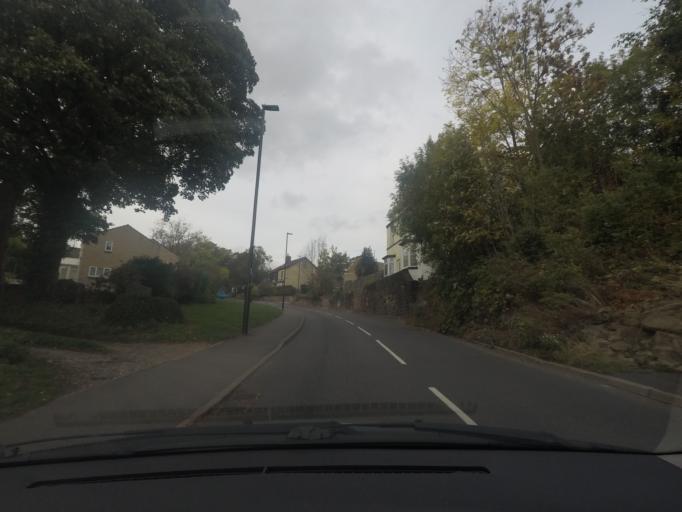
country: GB
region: England
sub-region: Sheffield
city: Oughtibridge
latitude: 53.4225
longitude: -1.4987
